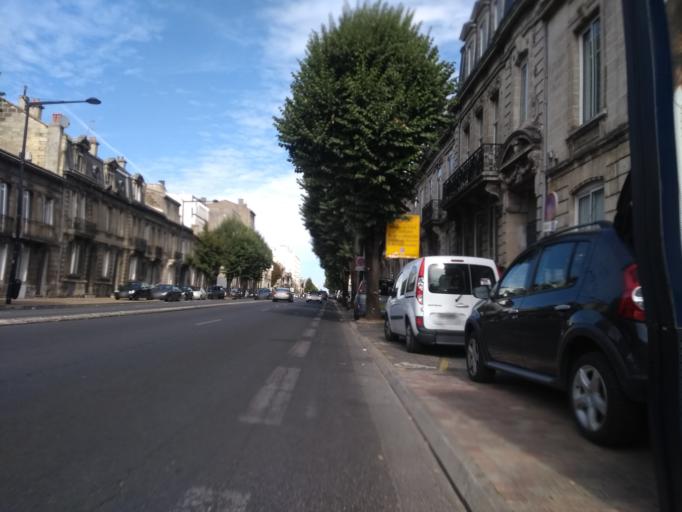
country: FR
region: Aquitaine
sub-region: Departement de la Gironde
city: Le Bouscat
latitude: 44.8487
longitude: -0.5971
